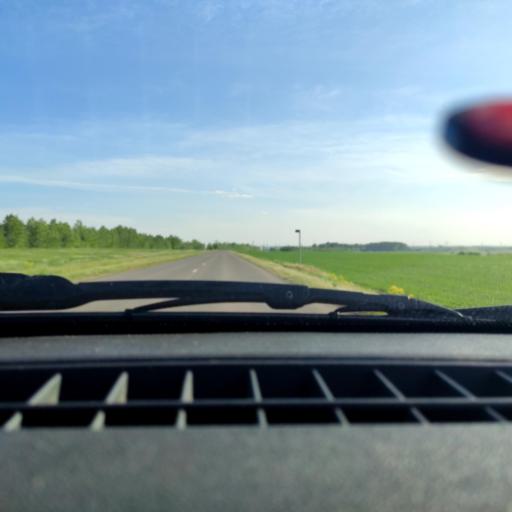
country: RU
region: Bashkortostan
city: Avdon
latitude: 54.4436
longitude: 55.8406
